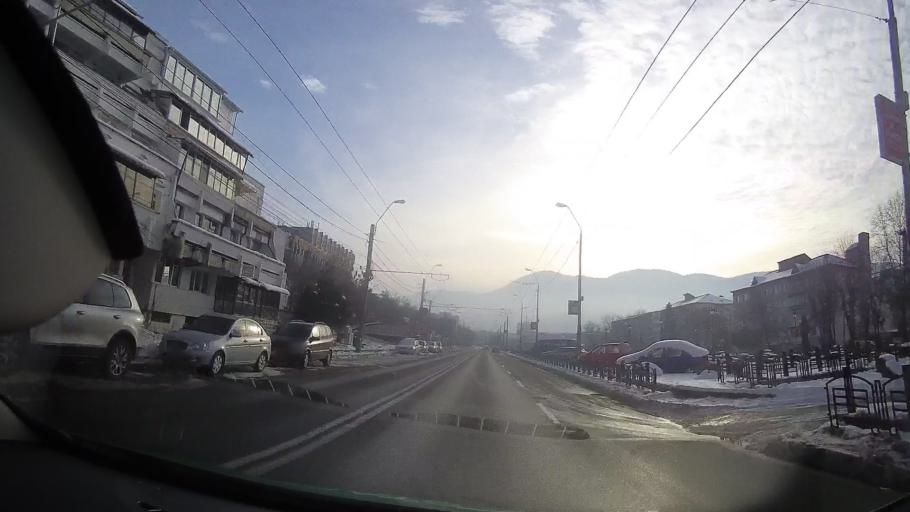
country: RO
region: Neamt
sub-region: Municipiul Piatra-Neamt
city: Valeni
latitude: 46.9304
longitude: 26.3730
